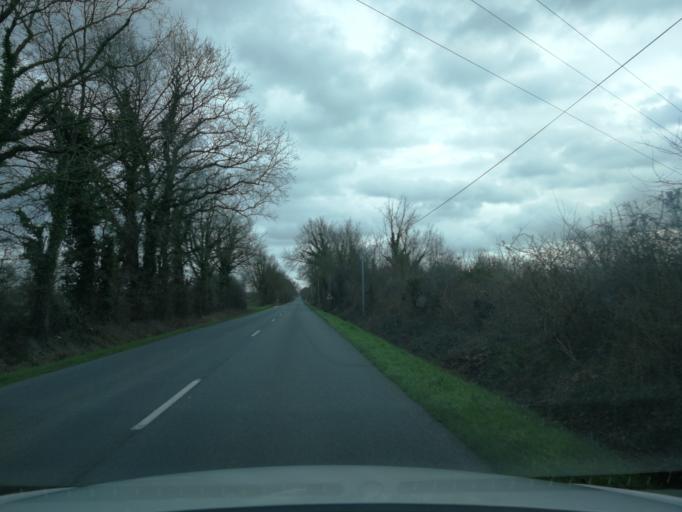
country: FR
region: Pays de la Loire
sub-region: Departement de la Loire-Atlantique
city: Montbert
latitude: 47.0277
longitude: -1.4967
